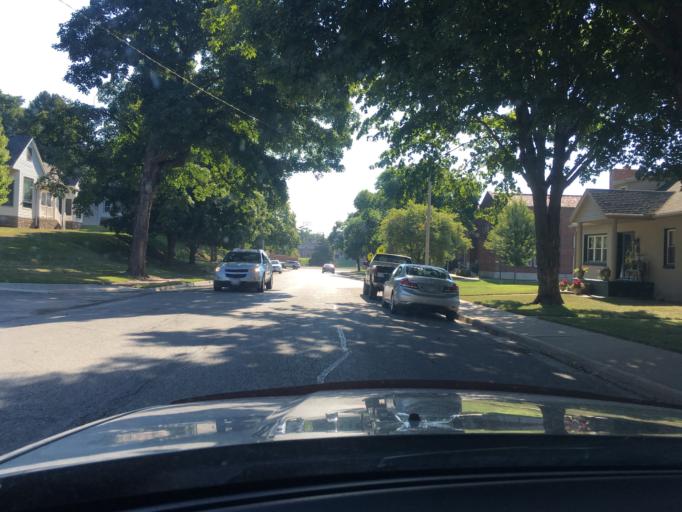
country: US
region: Kansas
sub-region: Atchison County
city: Atchison
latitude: 39.5720
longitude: -95.1167
